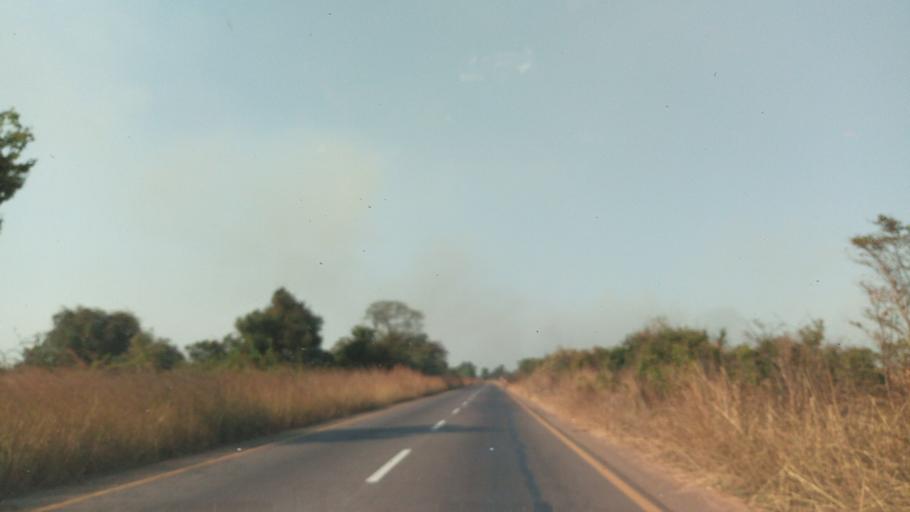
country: CD
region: Katanga
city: Lubumbashi
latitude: -11.4204
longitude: 27.7322
